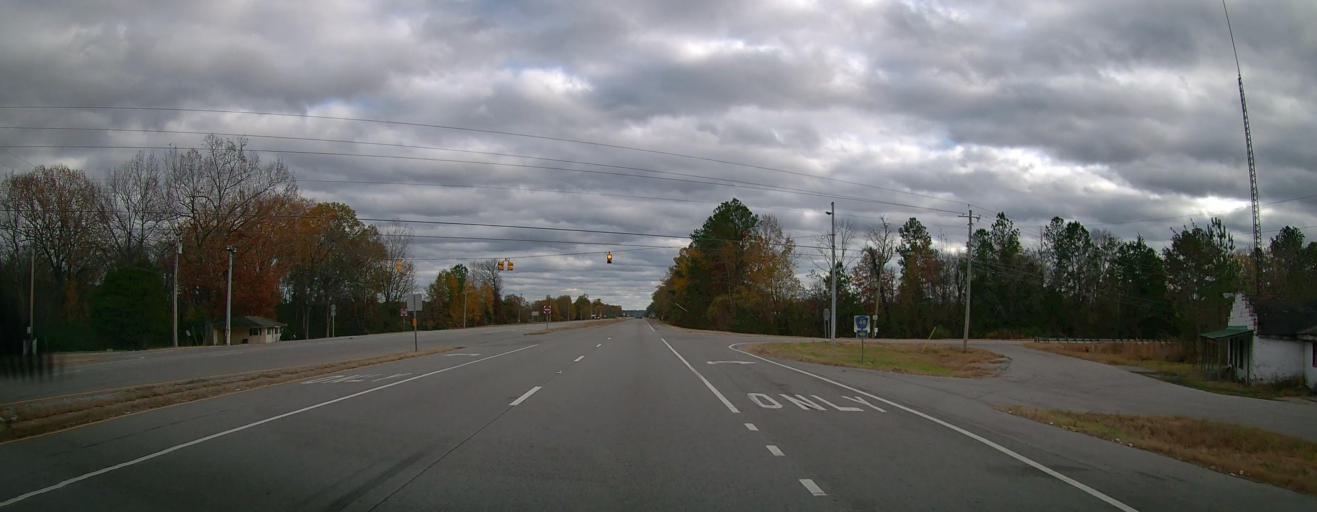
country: US
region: Alabama
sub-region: Lawrence County
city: Town Creek
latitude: 34.6539
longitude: -87.5296
